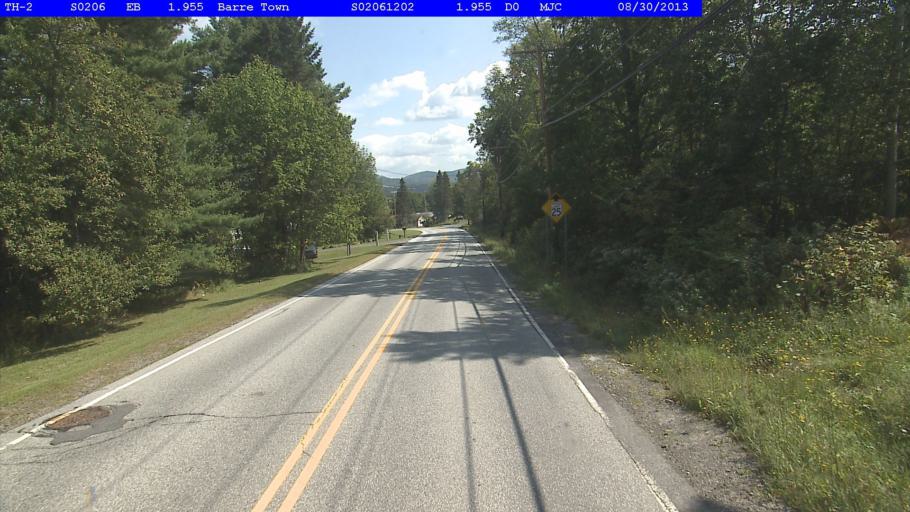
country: US
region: Vermont
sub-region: Washington County
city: South Barre
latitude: 44.1595
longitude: -72.4585
